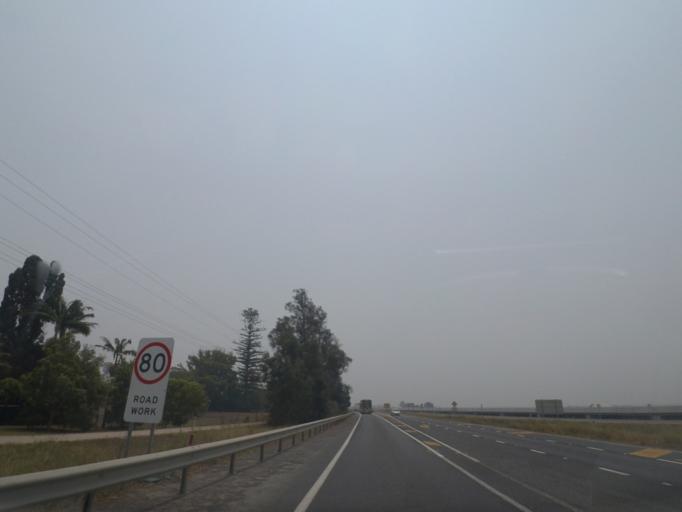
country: AU
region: New South Wales
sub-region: Clarence Valley
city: Maclean
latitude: -29.4184
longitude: 153.2408
